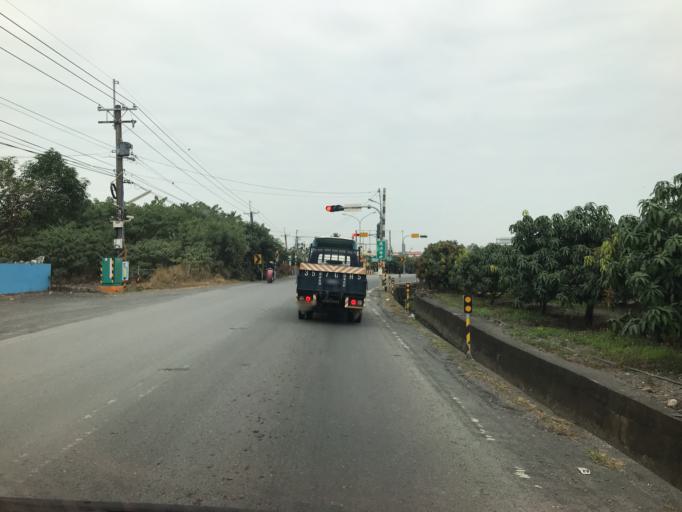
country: TW
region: Taiwan
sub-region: Pingtung
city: Pingtung
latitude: 22.5028
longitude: 120.5883
